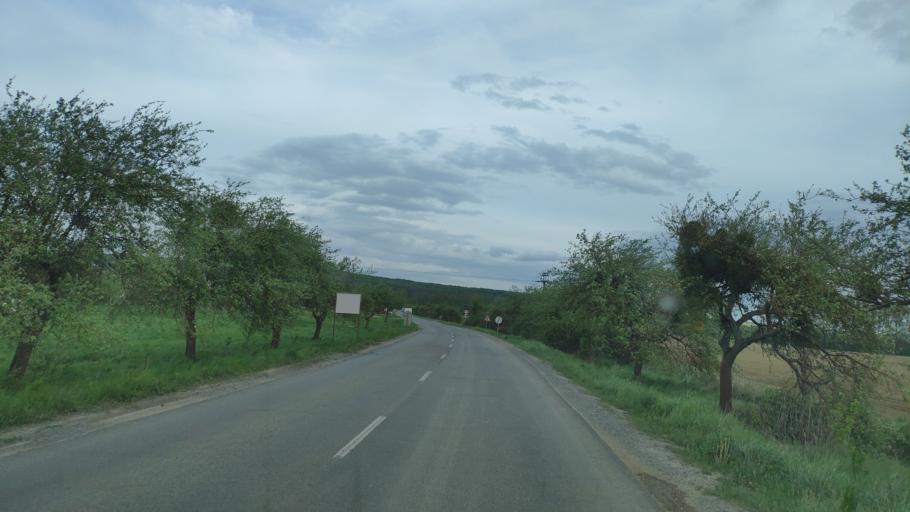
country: SK
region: Kosicky
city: Kosice
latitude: 48.7809
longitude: 21.3166
